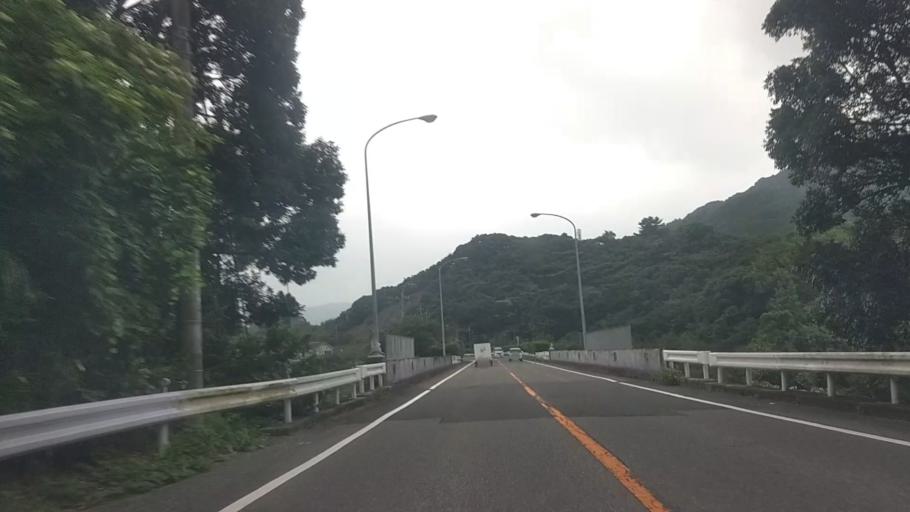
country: JP
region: Chiba
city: Kawaguchi
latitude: 35.1472
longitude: 140.0687
